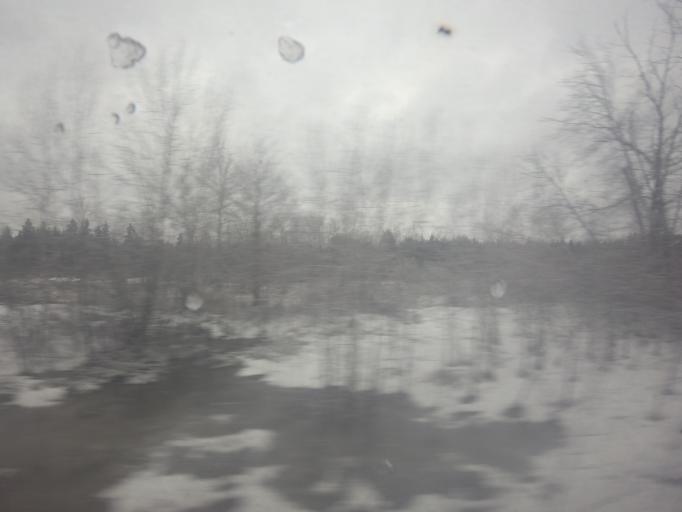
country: CA
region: Ontario
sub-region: Lanark County
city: Smiths Falls
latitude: 44.9494
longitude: -76.0133
